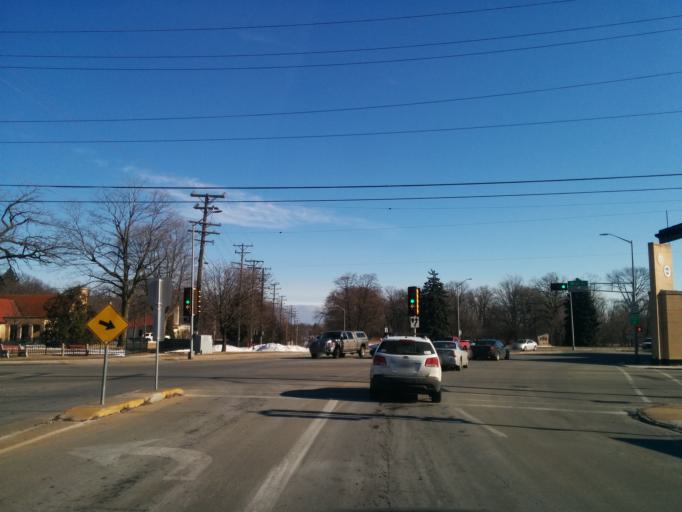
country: US
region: Wisconsin
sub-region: Racine County
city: Racine
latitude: 42.7187
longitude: -87.8166
